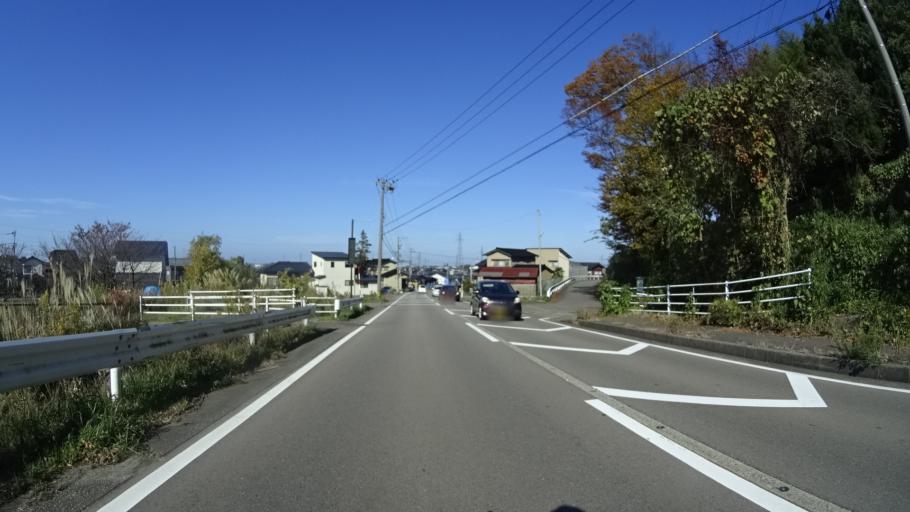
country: JP
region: Ishikawa
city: Tsurugi-asahimachi
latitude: 36.4815
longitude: 136.6158
